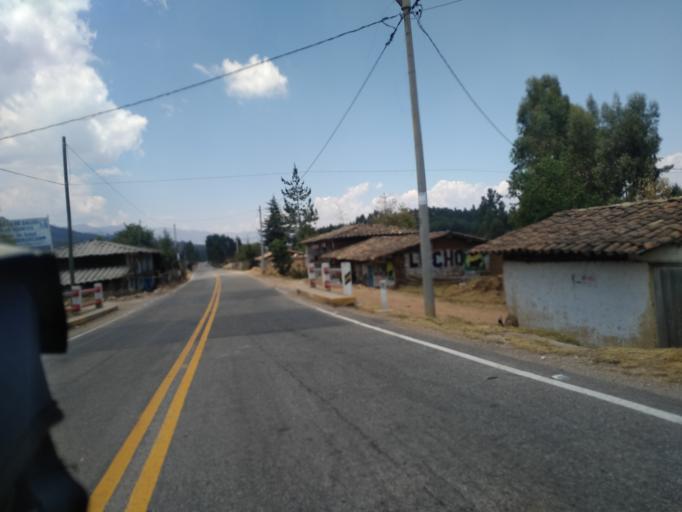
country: PE
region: Cajamarca
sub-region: San Marcos
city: San Marcos
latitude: -7.2794
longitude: -78.2369
